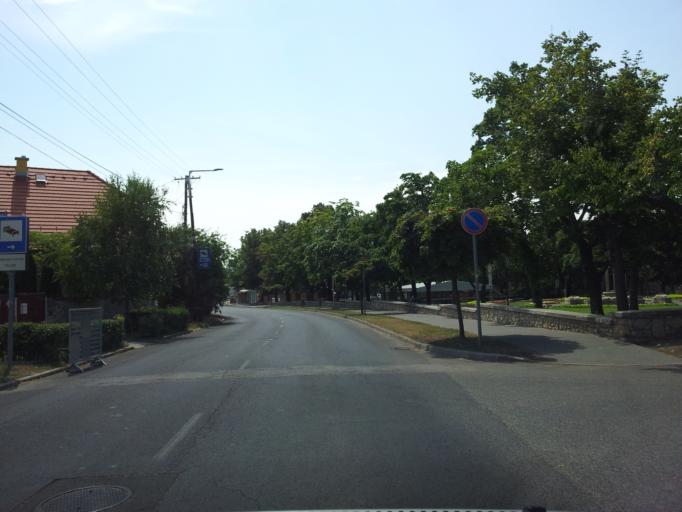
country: HU
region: Veszprem
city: Tapolca
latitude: 46.8855
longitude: 17.4436
